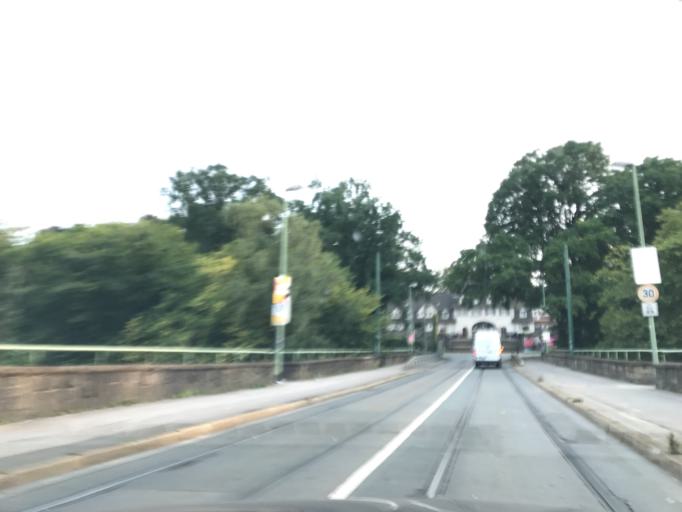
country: DE
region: North Rhine-Westphalia
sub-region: Regierungsbezirk Dusseldorf
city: Essen
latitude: 51.4355
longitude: 6.9799
